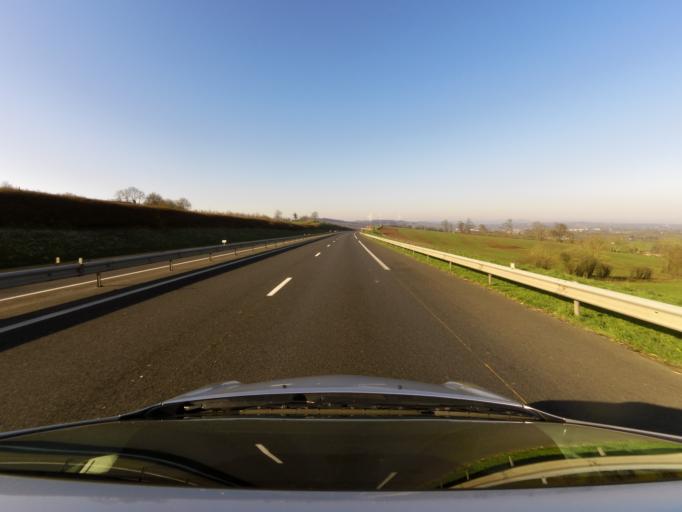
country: FR
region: Lower Normandy
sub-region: Departement de la Manche
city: Saint-Amand
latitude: 48.9962
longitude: -0.9158
